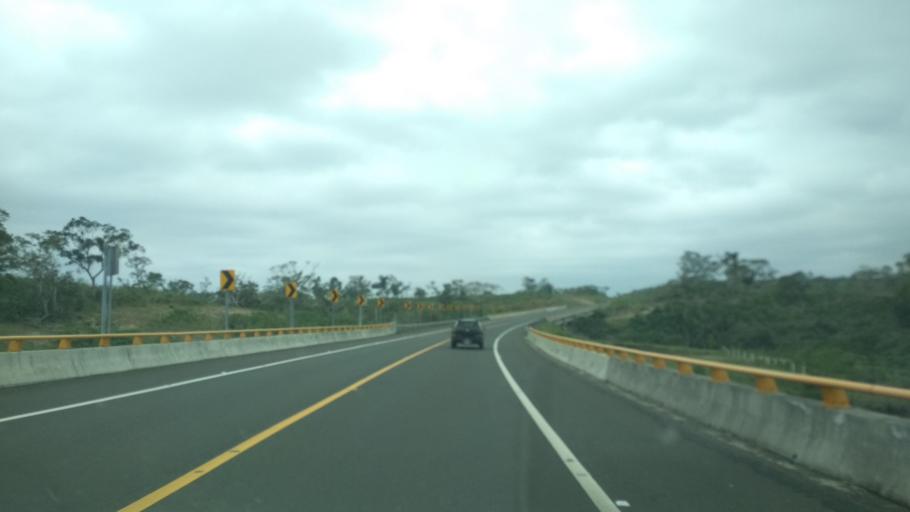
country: MX
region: Veracruz
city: Agua Dulce
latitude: 20.4265
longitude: -97.2254
